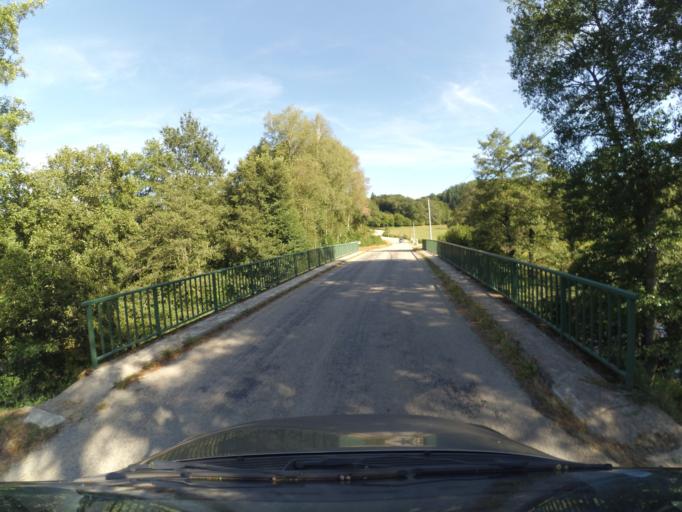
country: FR
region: Limousin
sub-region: Departement de la Correze
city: Bugeat
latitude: 45.7065
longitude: 1.8691
